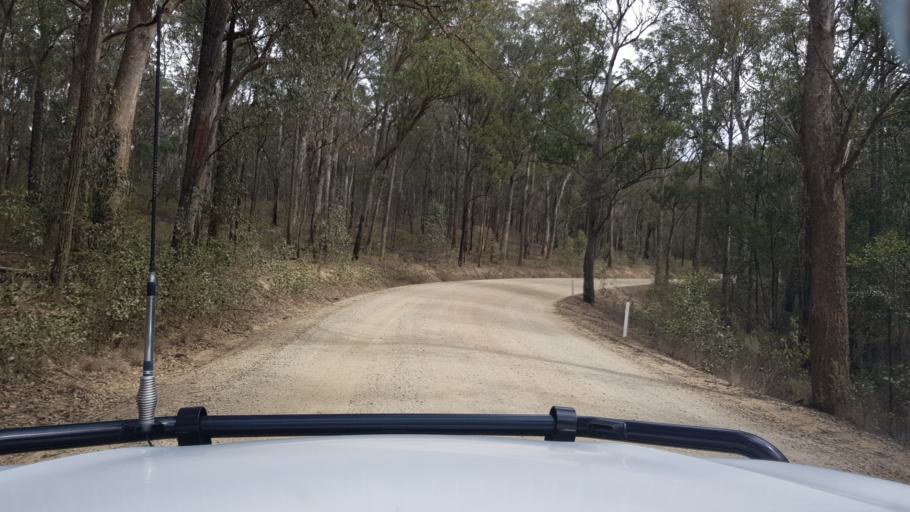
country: AU
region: Victoria
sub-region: East Gippsland
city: Bairnsdale
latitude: -37.7002
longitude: 147.5815
